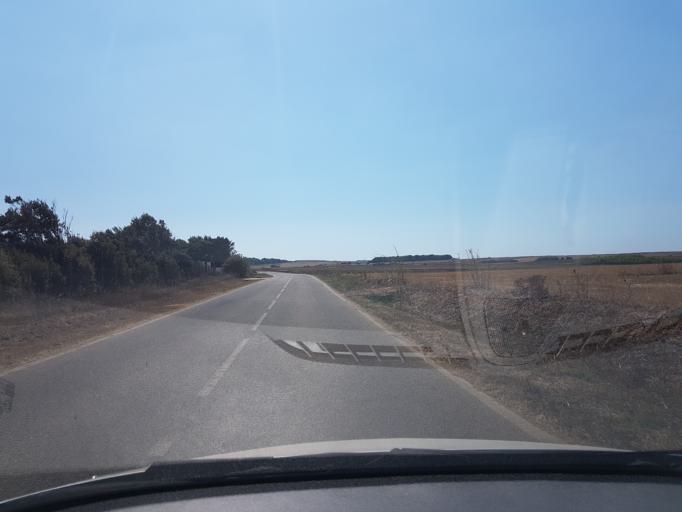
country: IT
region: Sardinia
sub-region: Provincia di Oristano
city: Riola Sardo
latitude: 39.9912
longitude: 8.4625
